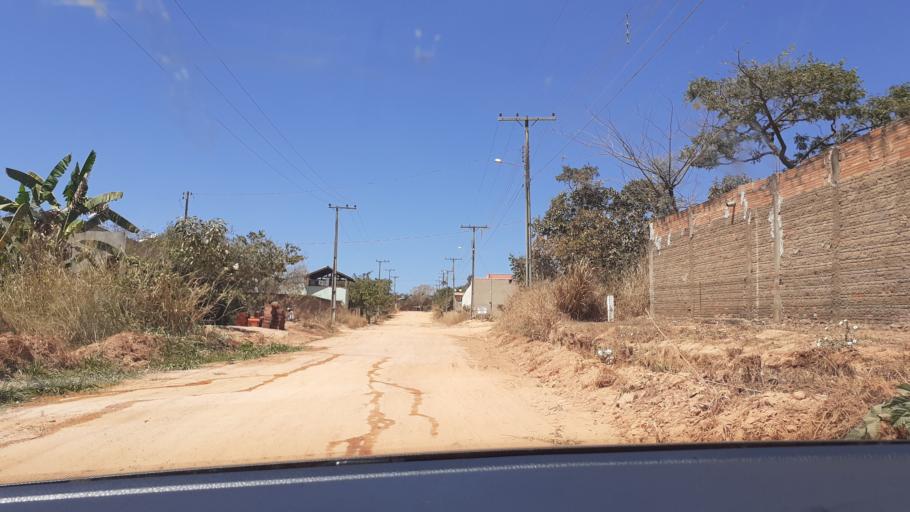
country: BR
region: Goias
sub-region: Caldas Novas
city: Caldas Novas
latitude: -17.7398
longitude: -48.6527
